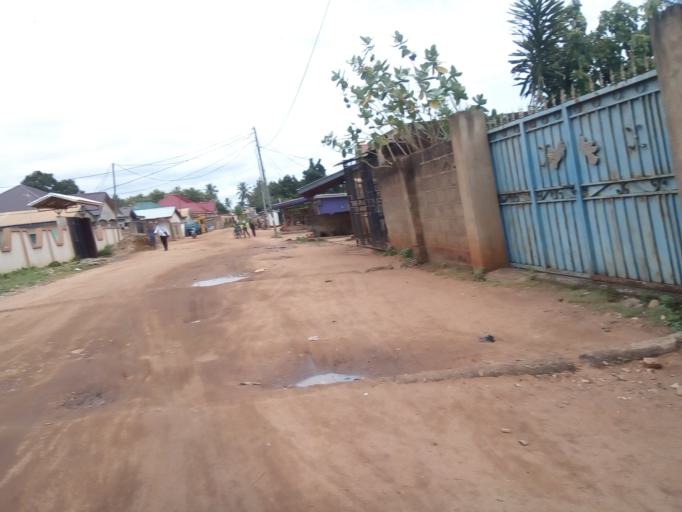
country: GH
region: Eastern
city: Nsawam
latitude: 5.7795
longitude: -0.3378
